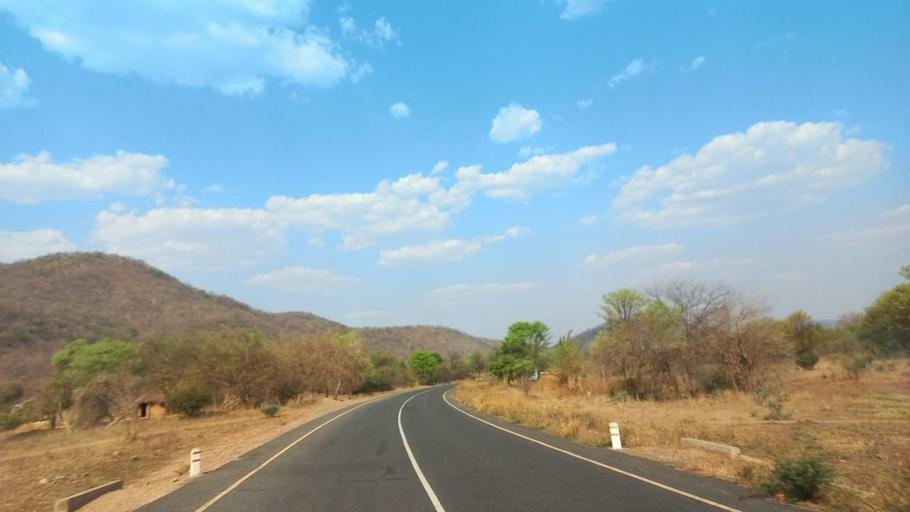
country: ZM
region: Lusaka
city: Luangwa
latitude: -15.0476
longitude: 30.2110
